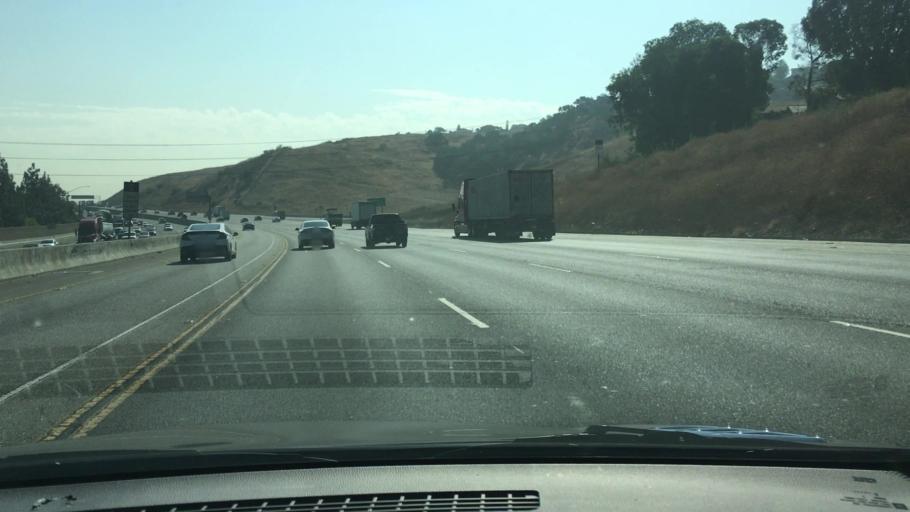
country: US
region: California
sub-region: San Bernardino County
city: Chino Hills
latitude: 34.0236
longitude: -117.7694
